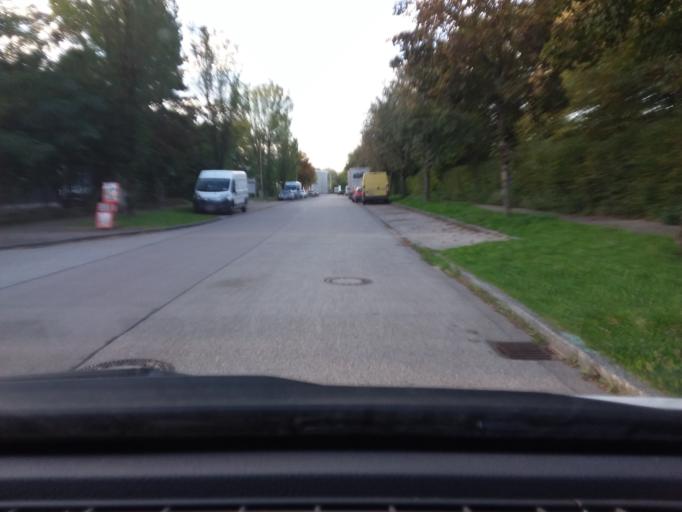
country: DE
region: Bavaria
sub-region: Upper Bavaria
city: Oberschleissheim
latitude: 48.2517
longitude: 11.6070
